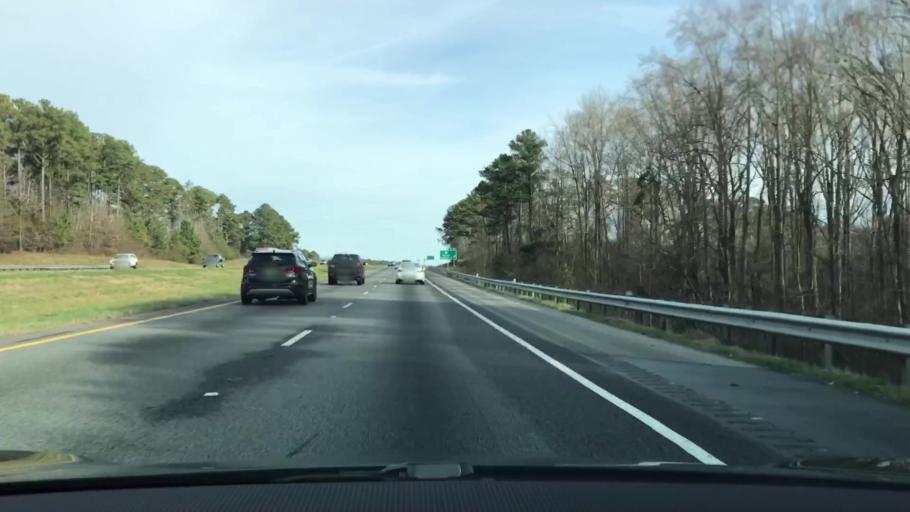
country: US
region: Georgia
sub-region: Walton County
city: Social Circle
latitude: 33.6117
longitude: -83.7595
